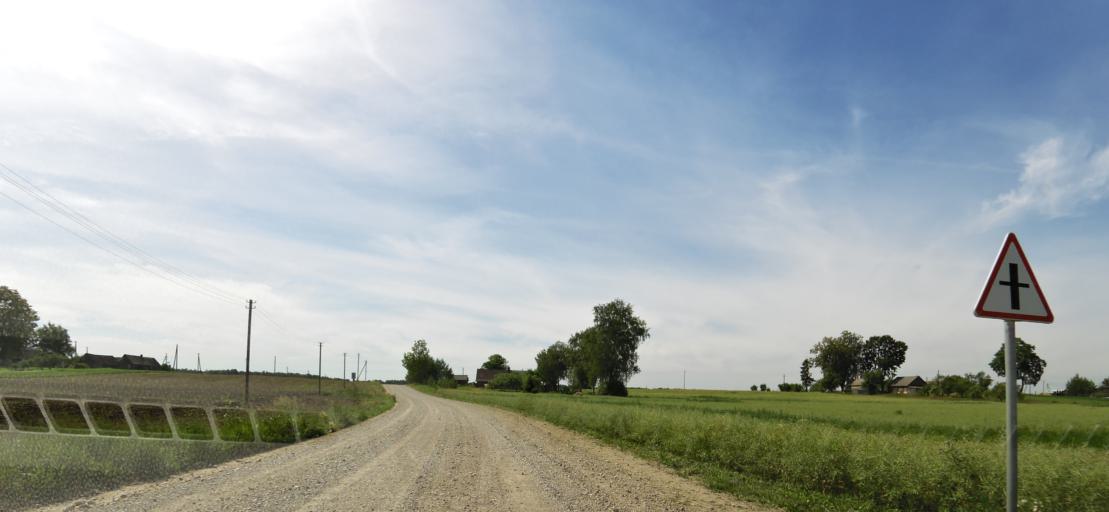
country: LT
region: Panevezys
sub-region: Panevezys City
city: Panevezys
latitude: 55.8843
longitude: 24.3335
